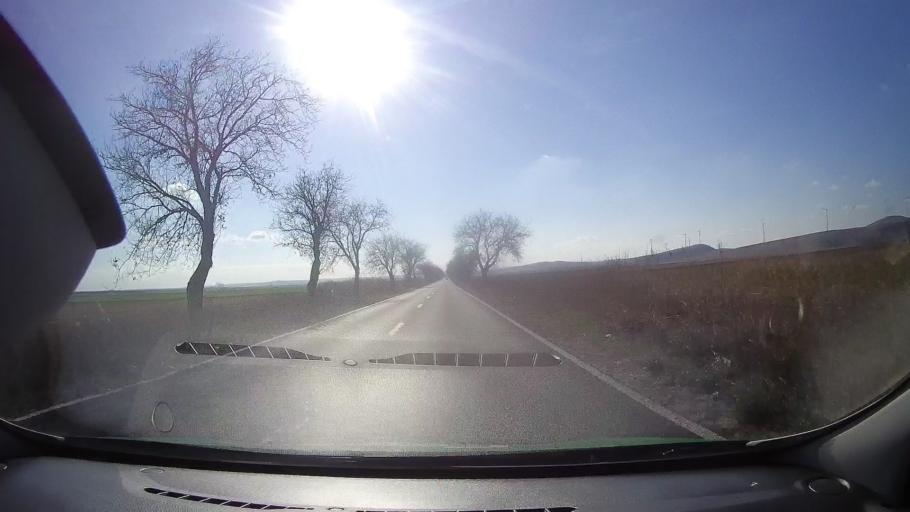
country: RO
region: Tulcea
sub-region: Comuna Ceamurlia de Jos
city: Ceamurlia de Jos
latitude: 44.7950
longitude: 28.6902
